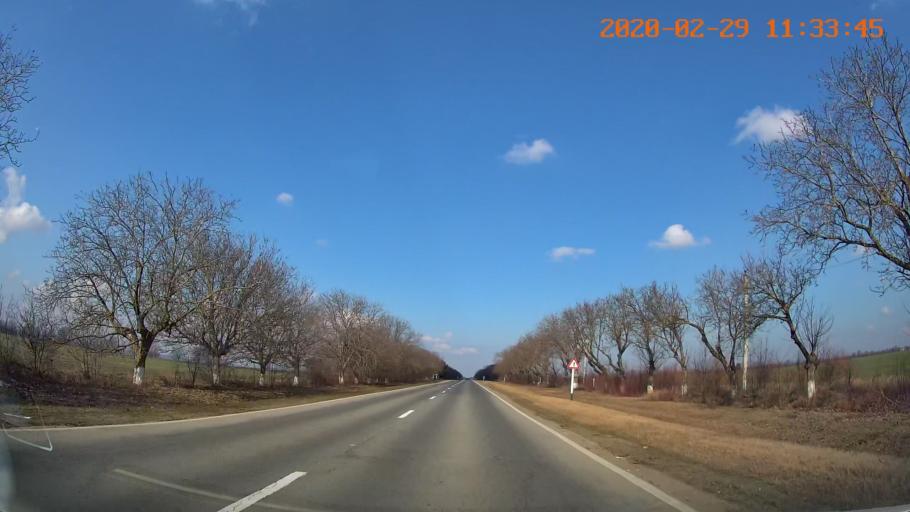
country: MD
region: Rezina
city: Saharna
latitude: 47.5560
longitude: 29.0811
